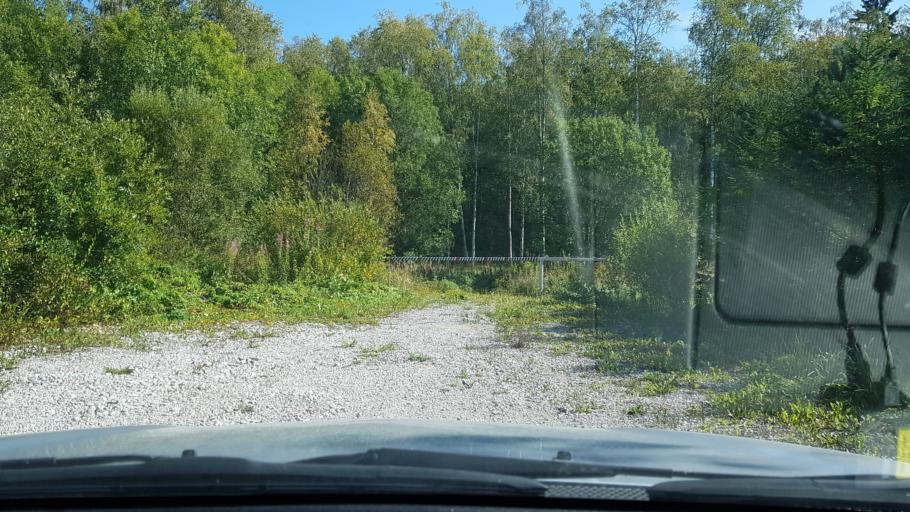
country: EE
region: Ida-Virumaa
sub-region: Sillamaee linn
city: Sillamae
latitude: 59.3712
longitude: 27.7976
